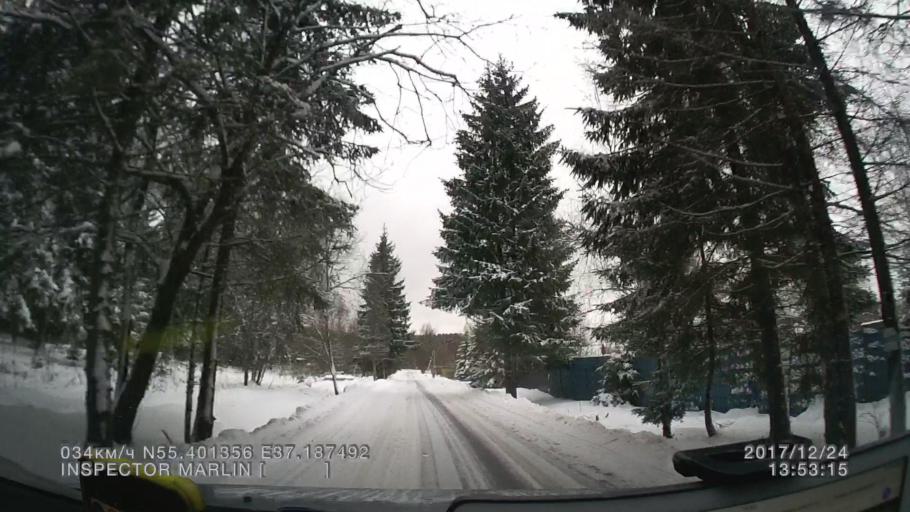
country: RU
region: Moskovskaya
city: Troitsk
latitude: 55.4014
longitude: 37.1874
